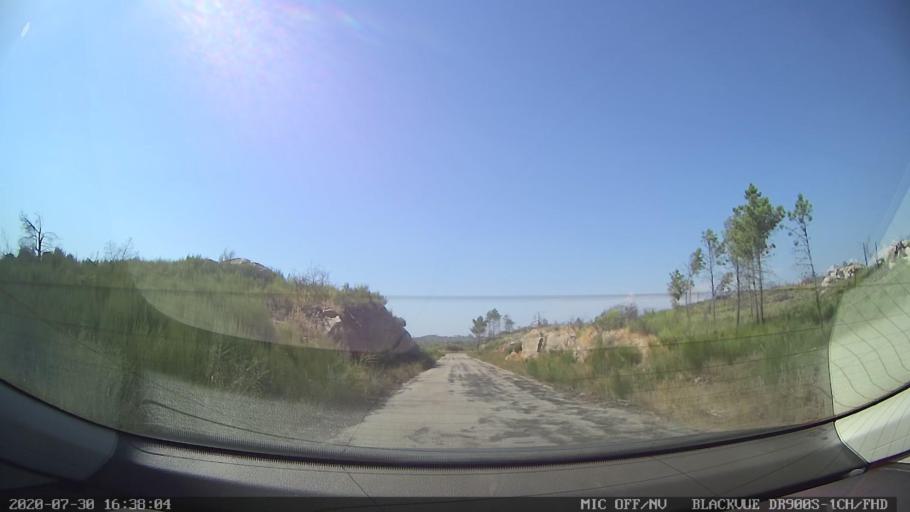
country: PT
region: Vila Real
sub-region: Sabrosa
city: Sabrosa
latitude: 41.3035
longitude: -7.4878
